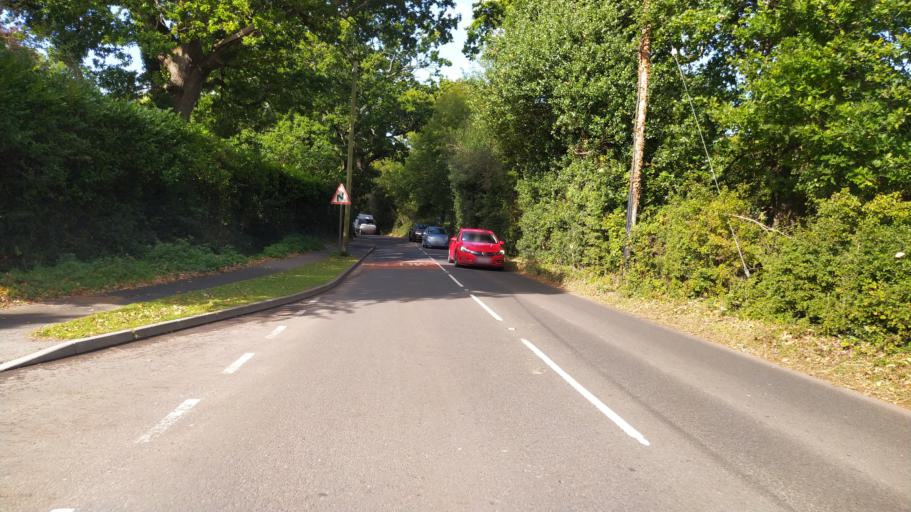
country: GB
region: England
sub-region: Hampshire
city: Bransgore
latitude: 50.8281
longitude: -1.7045
